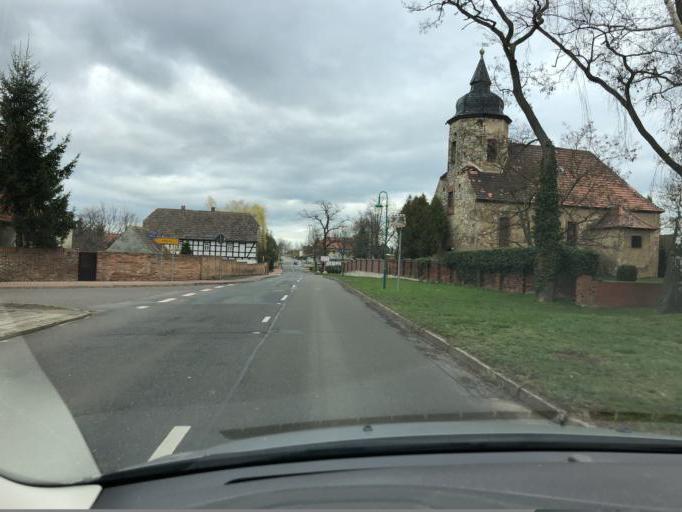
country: DE
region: Saxony-Anhalt
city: Muschwitz
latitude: 51.2160
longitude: 12.1401
